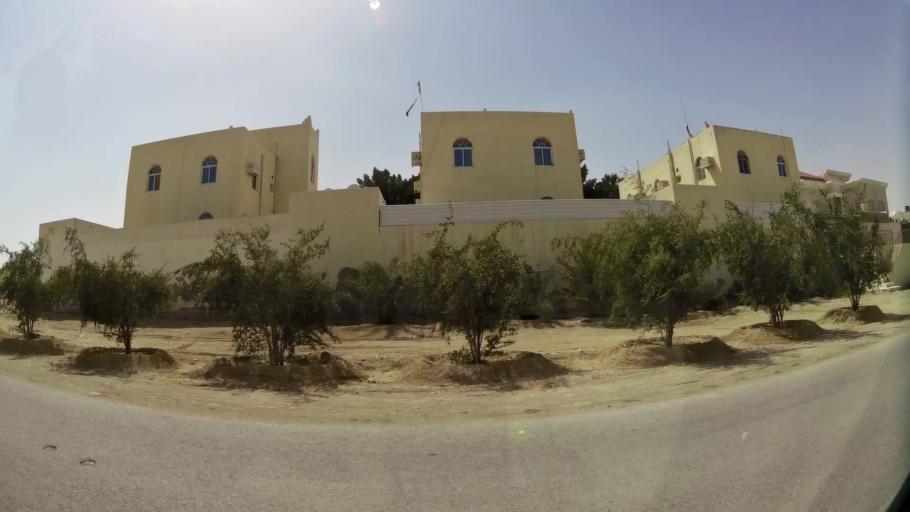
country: QA
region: Baladiyat Umm Salal
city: Umm Salal Muhammad
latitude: 25.3841
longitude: 51.4182
